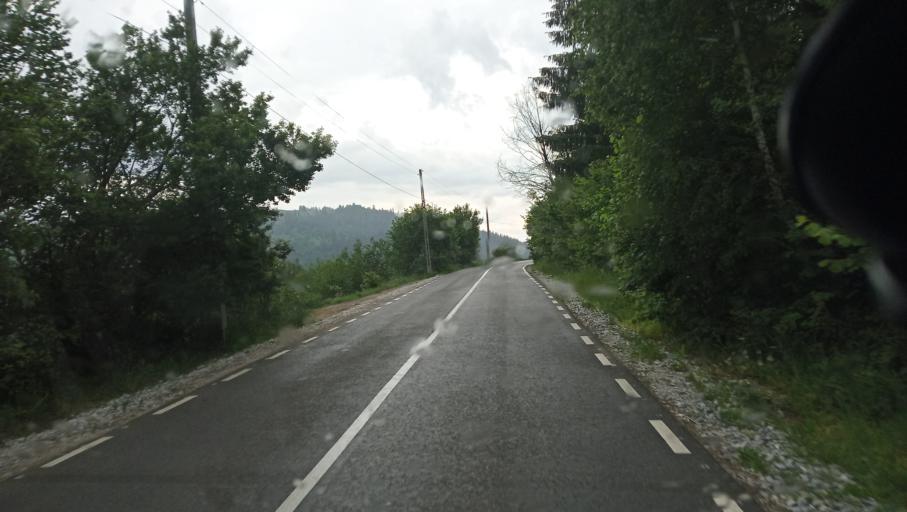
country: RO
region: Neamt
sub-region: Comuna Ceahlau
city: Ceahlau
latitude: 47.0545
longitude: 25.9490
